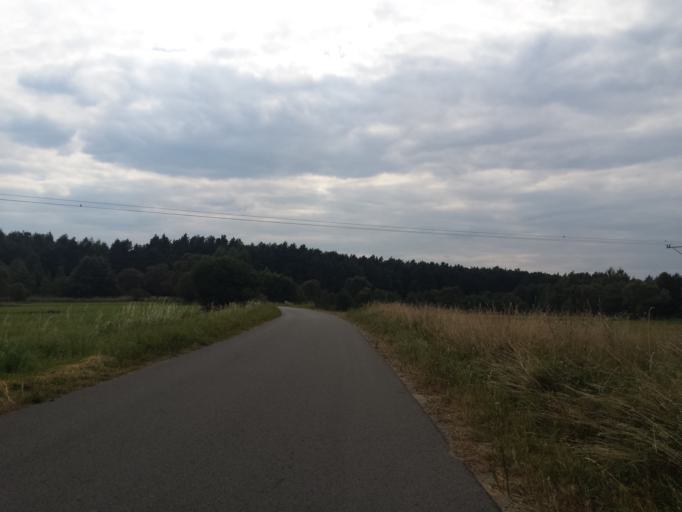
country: PL
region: Swietokrzyskie
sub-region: Powiat staszowski
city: Bogoria
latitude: 50.6574
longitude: 21.2265
